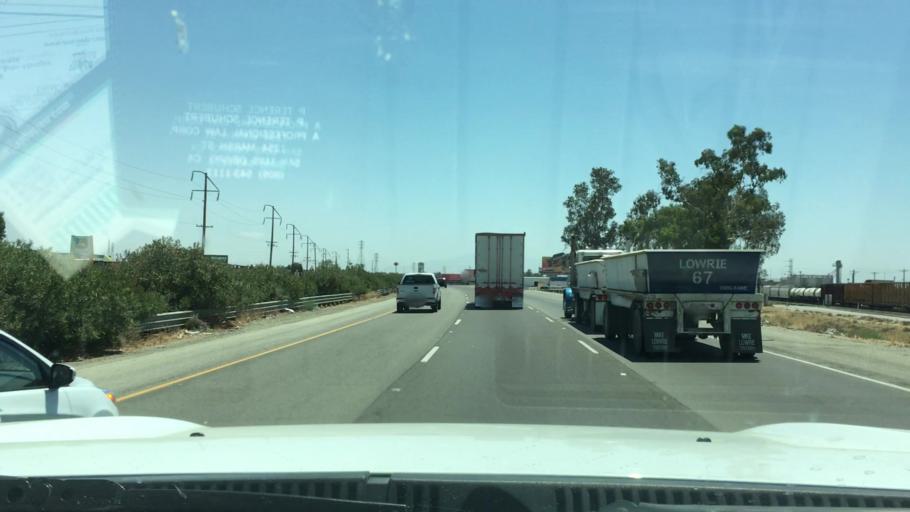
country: US
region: California
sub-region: Kern County
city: Greenacres
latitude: 35.4453
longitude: -119.0922
